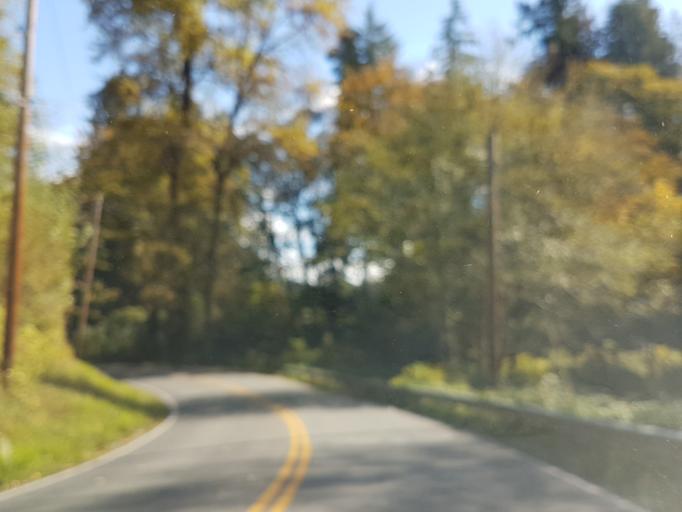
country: US
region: Washington
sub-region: Snohomish County
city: Cathcart
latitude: 47.8431
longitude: -122.0923
